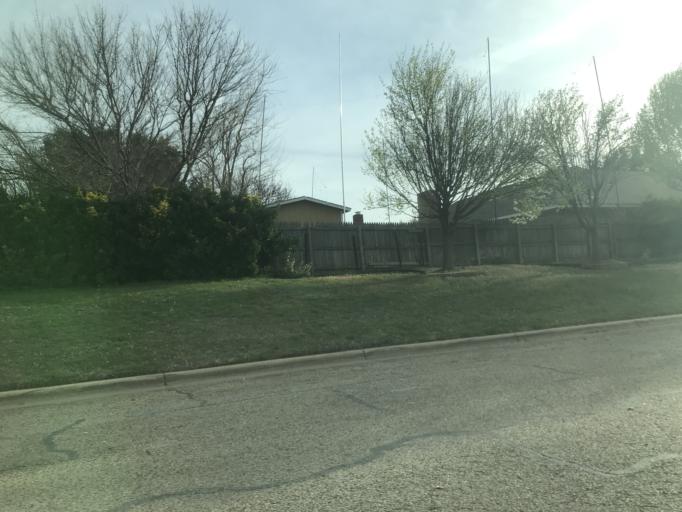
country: US
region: Texas
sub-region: Taylor County
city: Abilene
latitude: 32.3981
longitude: -99.7718
